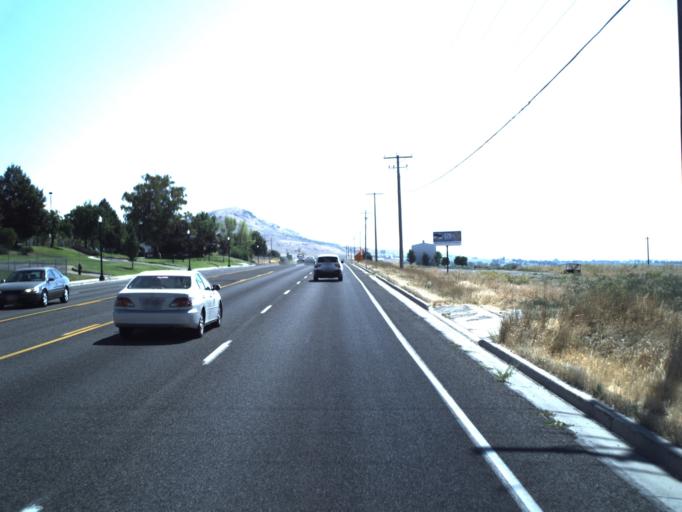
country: US
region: Utah
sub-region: Cache County
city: Richmond
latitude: 41.9127
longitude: -111.8147
